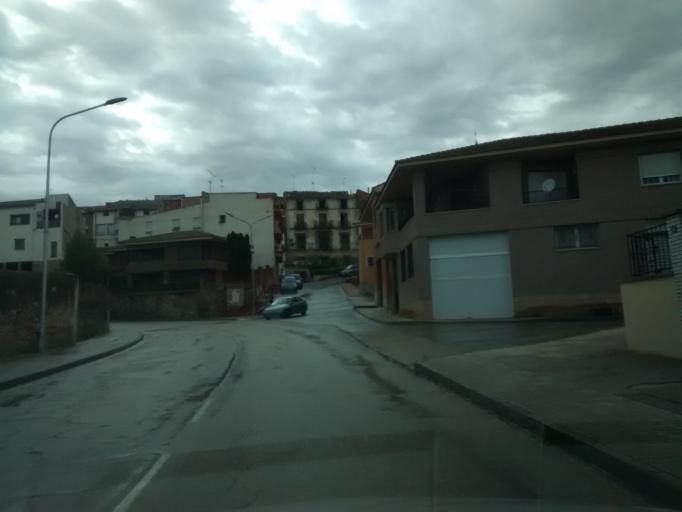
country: ES
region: Aragon
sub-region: Provincia de Zaragoza
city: Maella
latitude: 41.1207
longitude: 0.1405
